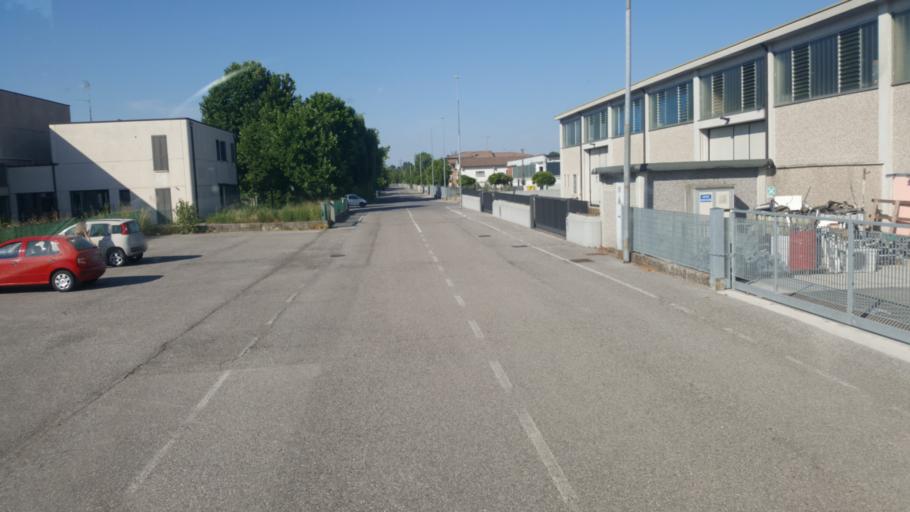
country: IT
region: Lombardy
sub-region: Provincia di Mantova
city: Asola
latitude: 45.2155
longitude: 10.3966
